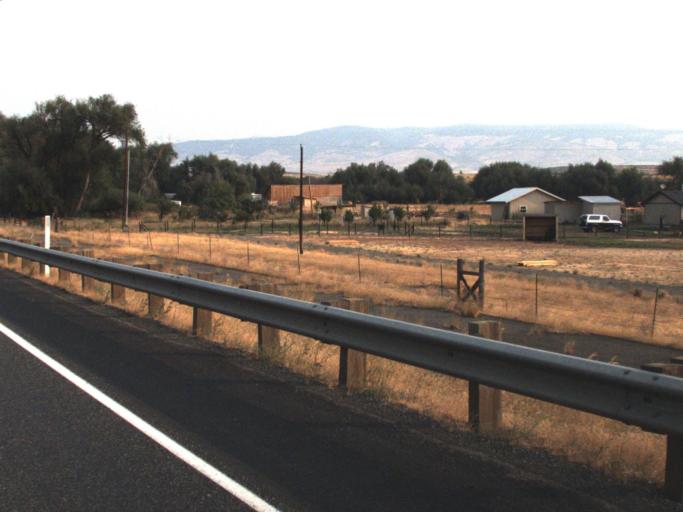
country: US
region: Washington
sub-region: Kittitas County
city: Ellensburg
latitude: 47.0632
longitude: -120.6221
